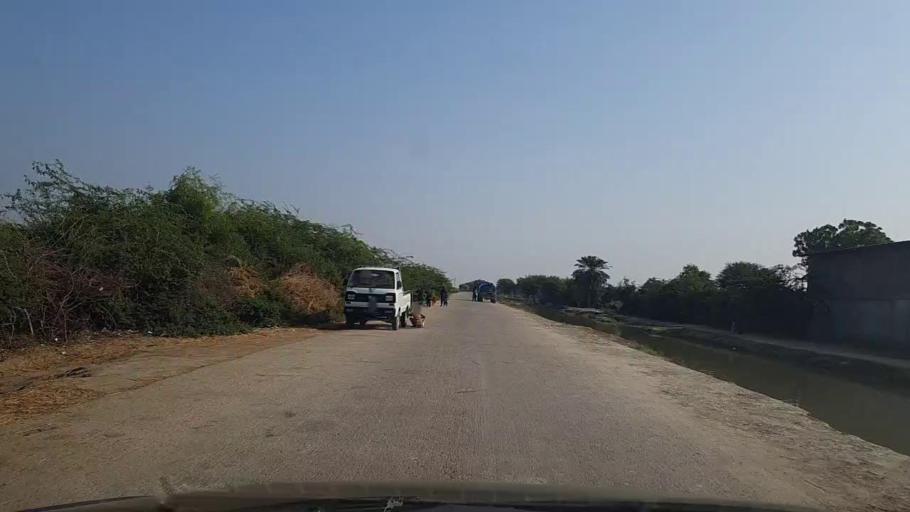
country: PK
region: Sindh
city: Thatta
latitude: 24.5919
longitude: 68.0779
